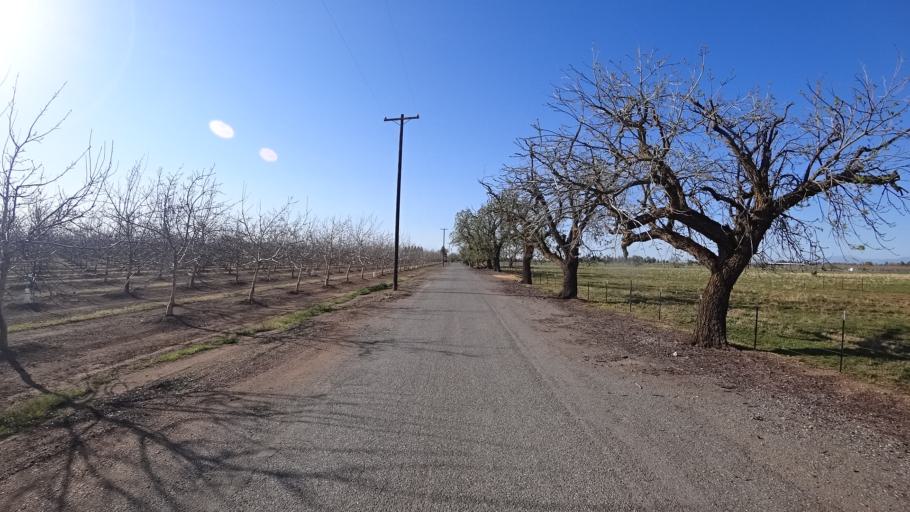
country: US
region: California
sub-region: Glenn County
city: Orland
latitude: 39.7600
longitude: -122.1134
